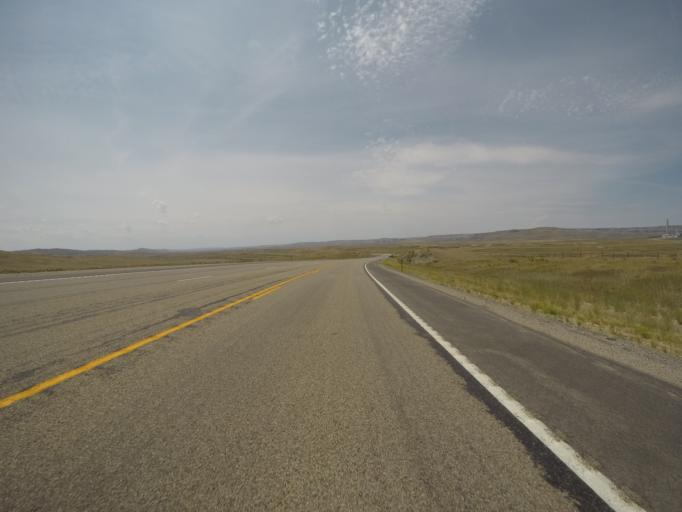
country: US
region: Wyoming
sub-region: Lincoln County
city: Kemmerer
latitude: 41.7574
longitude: -110.5608
